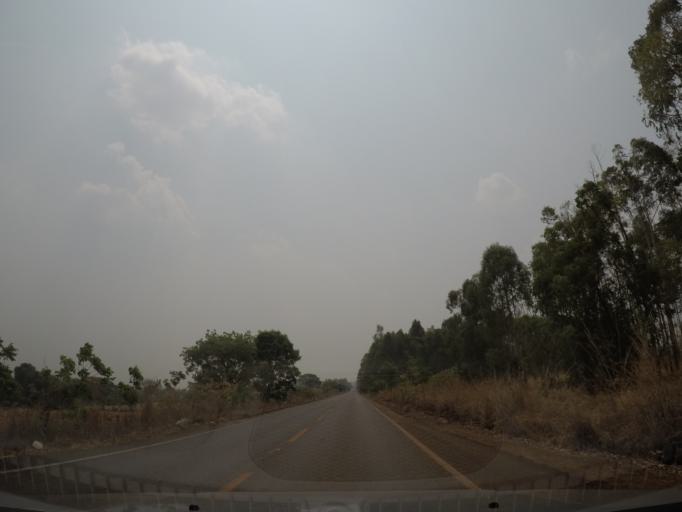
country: BR
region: Goias
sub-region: Pirenopolis
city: Pirenopolis
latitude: -15.9152
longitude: -48.8583
